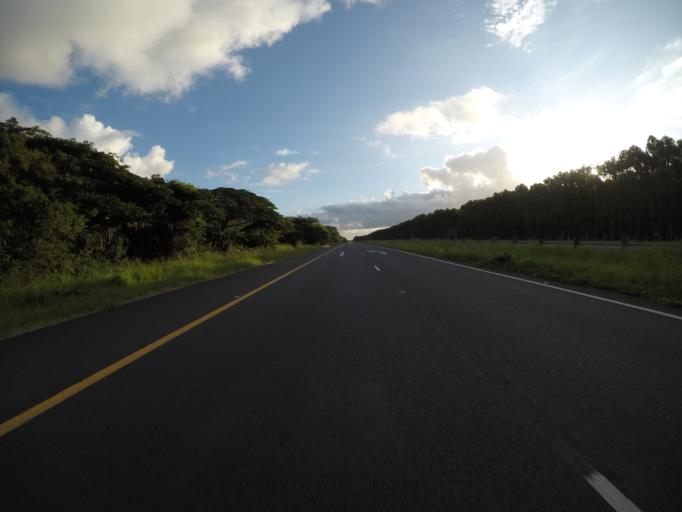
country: ZA
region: KwaZulu-Natal
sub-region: uThungulu District Municipality
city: KwaMbonambi
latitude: -28.5288
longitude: 32.1369
